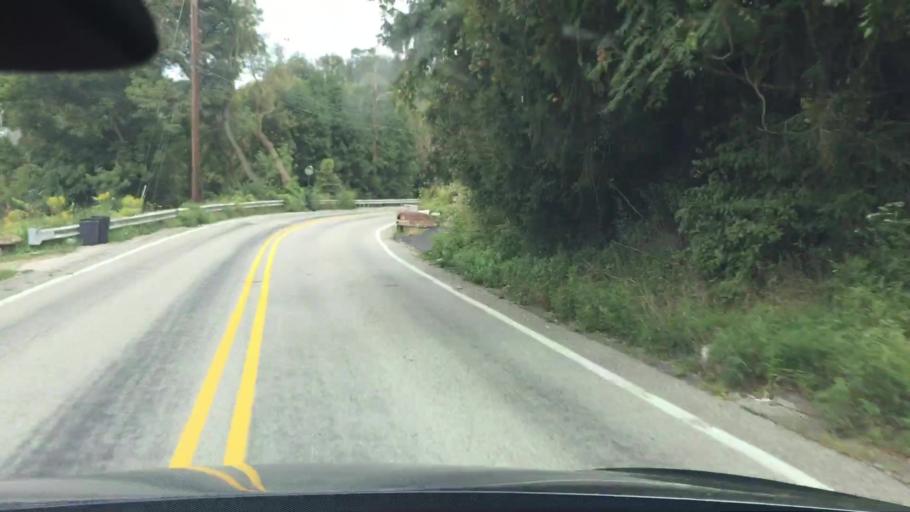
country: US
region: Pennsylvania
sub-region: Allegheny County
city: Penn Hills
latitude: 40.4879
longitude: -79.8210
